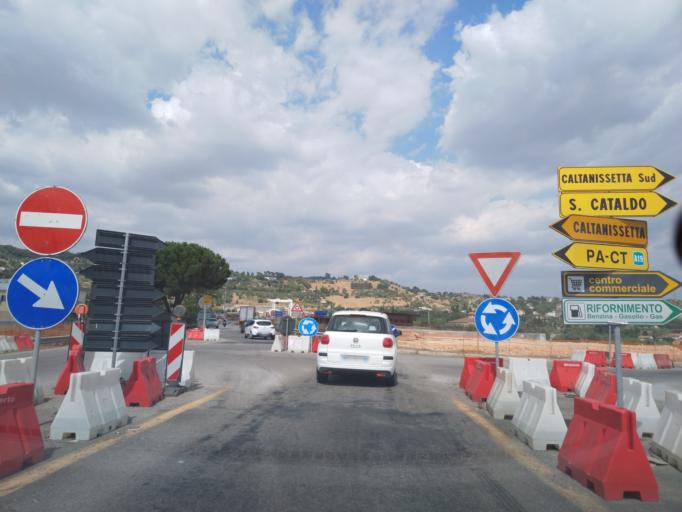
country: IT
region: Sicily
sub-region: Provincia di Caltanissetta
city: San Cataldo
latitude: 37.4718
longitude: 14.0115
